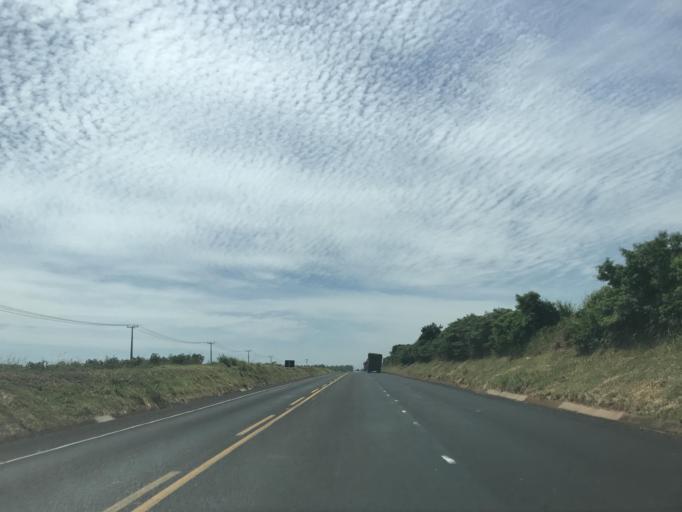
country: BR
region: Parana
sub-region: Paranavai
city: Paranavai
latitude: -23.0030
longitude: -52.5545
